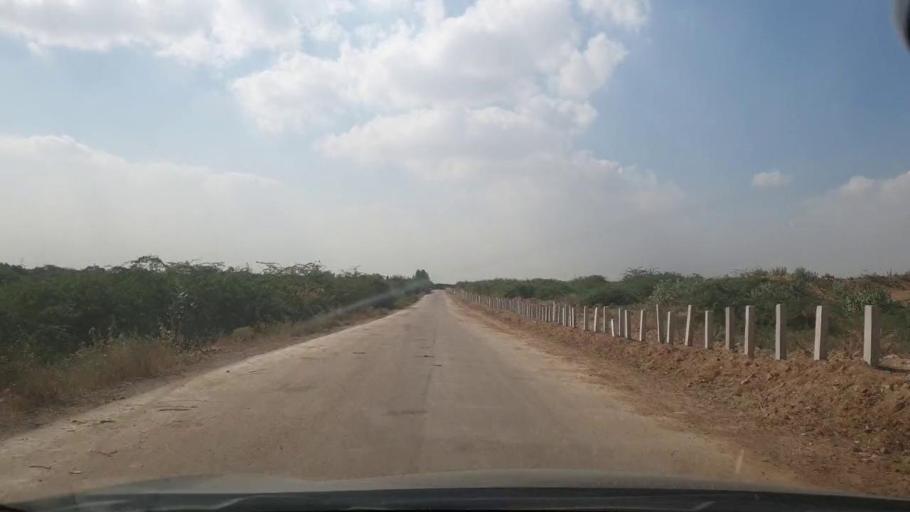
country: PK
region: Sindh
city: Malir Cantonment
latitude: 25.0245
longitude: 67.3583
